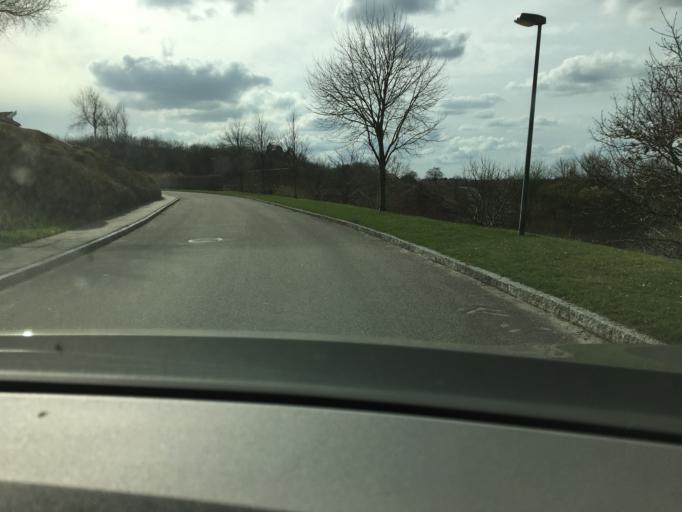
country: DK
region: South Denmark
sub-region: Vejle Kommune
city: Vejle
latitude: 55.7257
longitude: 9.5152
